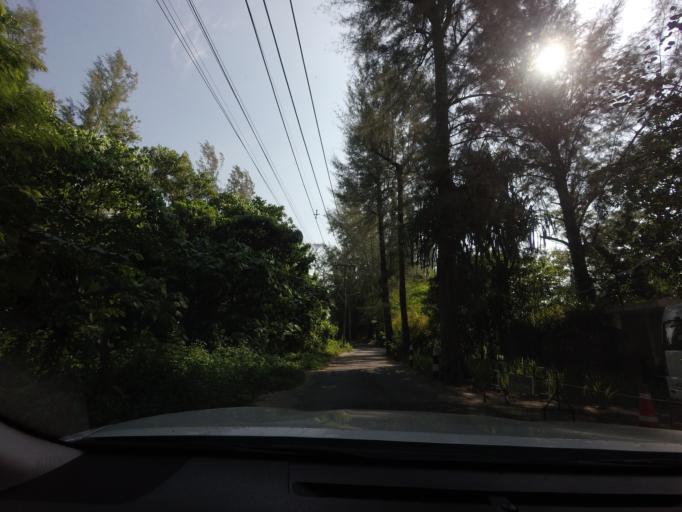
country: TH
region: Phangnga
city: Ban Khao Lak
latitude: 8.7349
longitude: 98.2426
